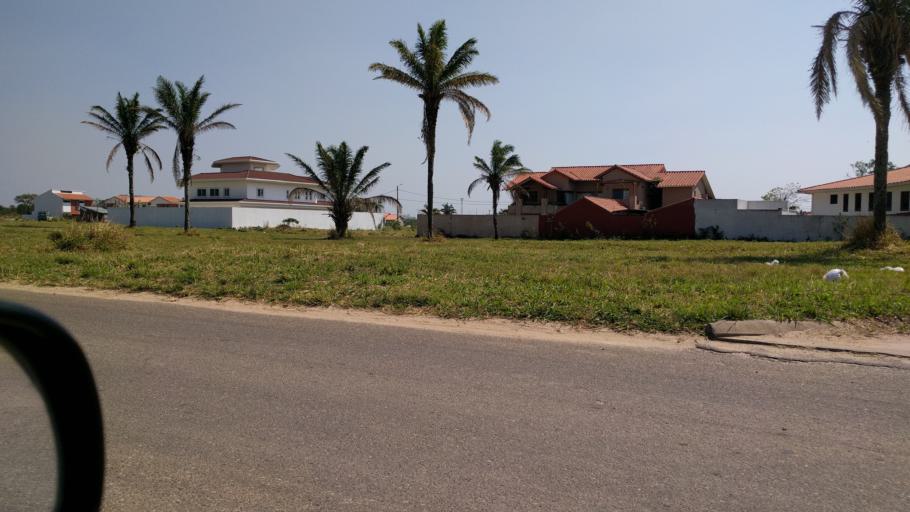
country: BO
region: Santa Cruz
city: Santa Cruz de la Sierra
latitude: -17.7533
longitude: -63.2298
